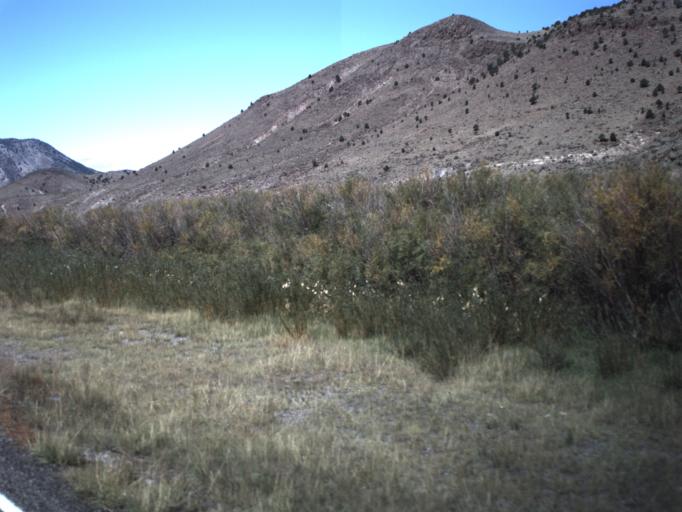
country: US
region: Utah
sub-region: Piute County
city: Junction
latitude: 38.1652
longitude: -112.0338
